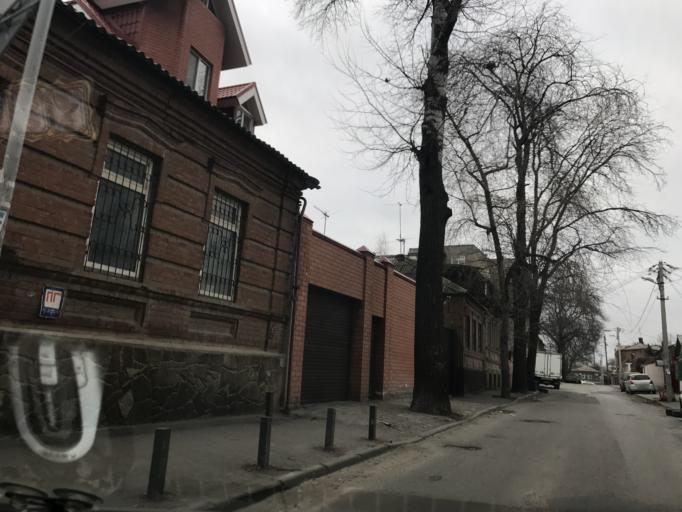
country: RU
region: Rostov
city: Rostov-na-Donu
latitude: 47.2237
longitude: 39.7375
